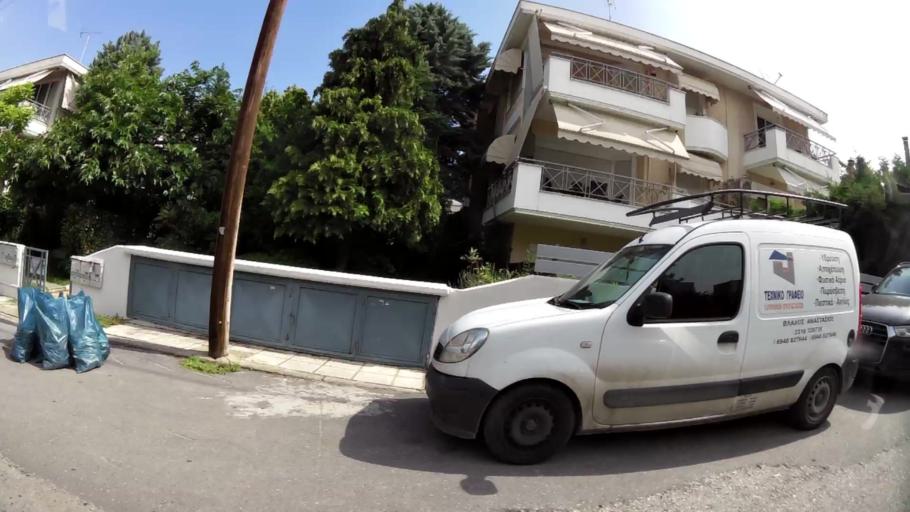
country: GR
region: Central Macedonia
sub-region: Nomos Thessalonikis
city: Panorama
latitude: 40.5833
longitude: 23.0163
